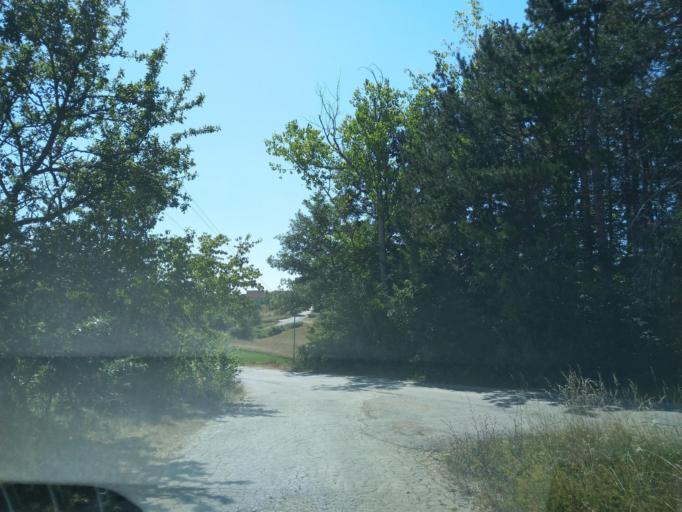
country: RS
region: Central Serbia
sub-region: Zlatiborski Okrug
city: Uzice
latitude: 43.8053
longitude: 19.8404
